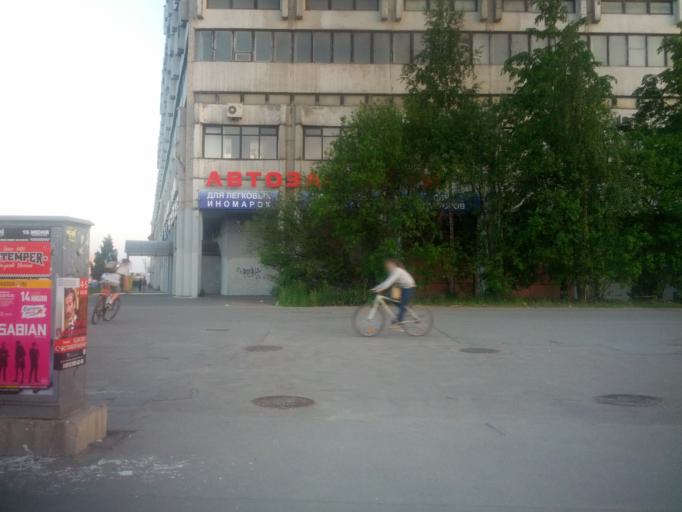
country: RU
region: St.-Petersburg
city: Staraya Derevnya
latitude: 59.9955
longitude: 30.2533
